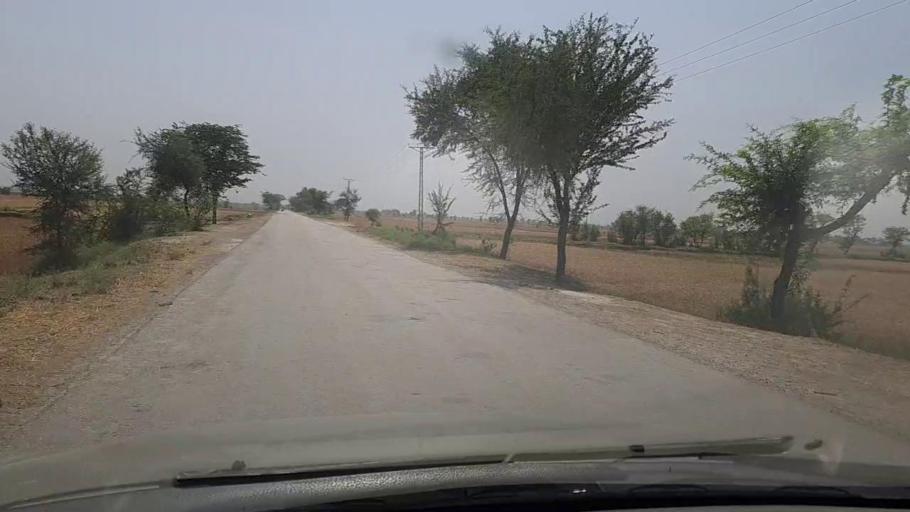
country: PK
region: Sindh
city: Miro Khan
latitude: 27.7033
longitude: 68.0619
